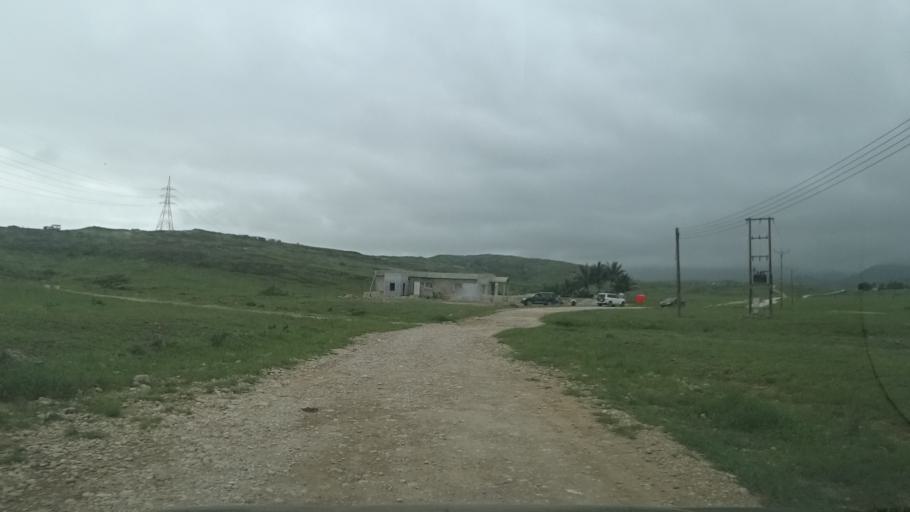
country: OM
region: Zufar
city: Salalah
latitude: 17.1130
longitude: 54.2346
